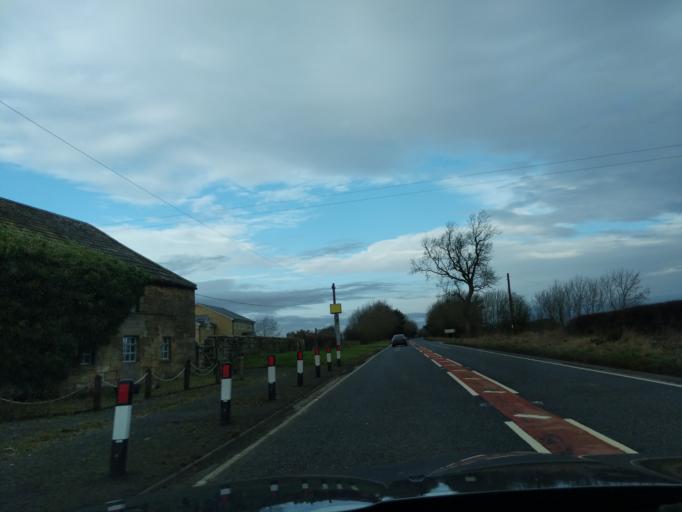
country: GB
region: England
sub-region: Northumberland
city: Meldon
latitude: 55.0845
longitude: -1.8090
